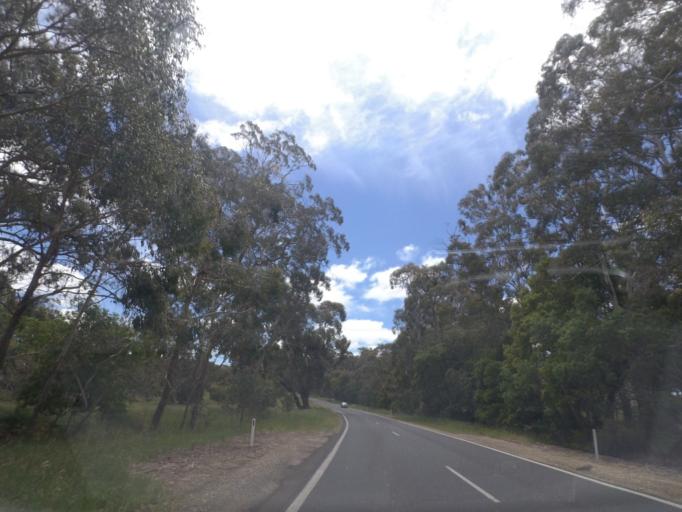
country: AU
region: Victoria
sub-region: Mount Alexander
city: Castlemaine
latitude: -37.3313
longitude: 144.1668
